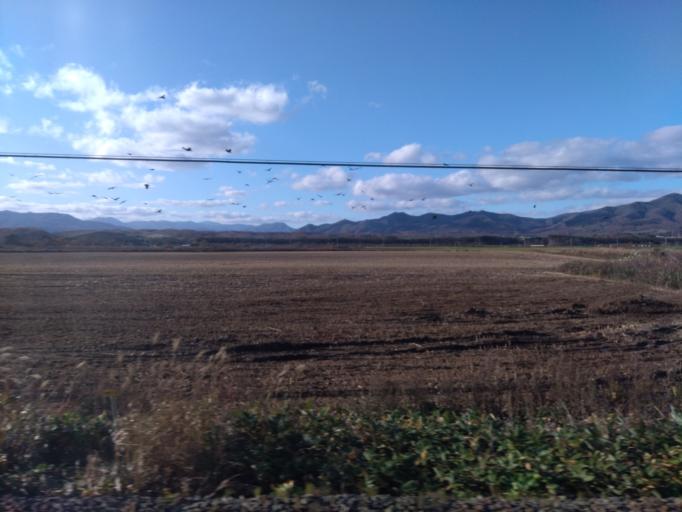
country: JP
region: Hokkaido
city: Niseko Town
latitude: 42.5410
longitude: 140.4068
